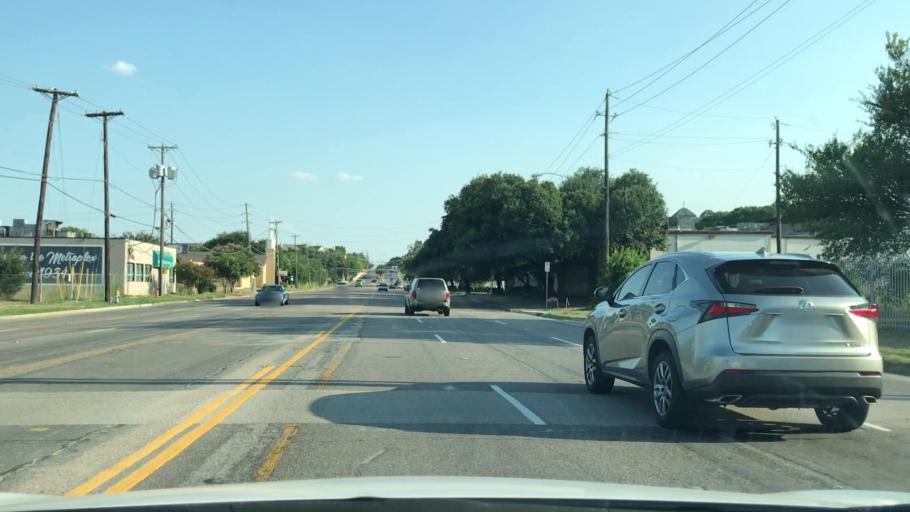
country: US
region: Texas
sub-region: Dallas County
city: Dallas
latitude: 32.7682
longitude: -96.8229
